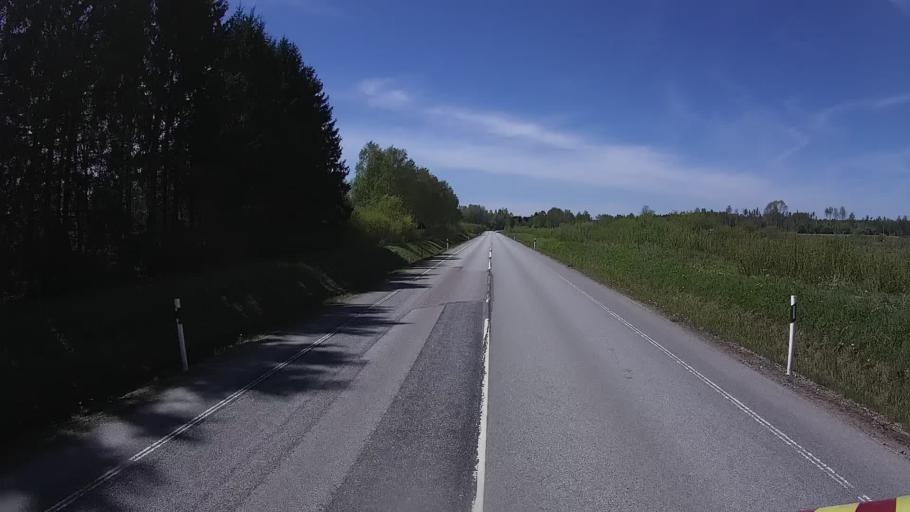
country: EE
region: Vorumaa
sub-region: Voru linn
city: Voru
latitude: 57.8900
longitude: 27.1751
